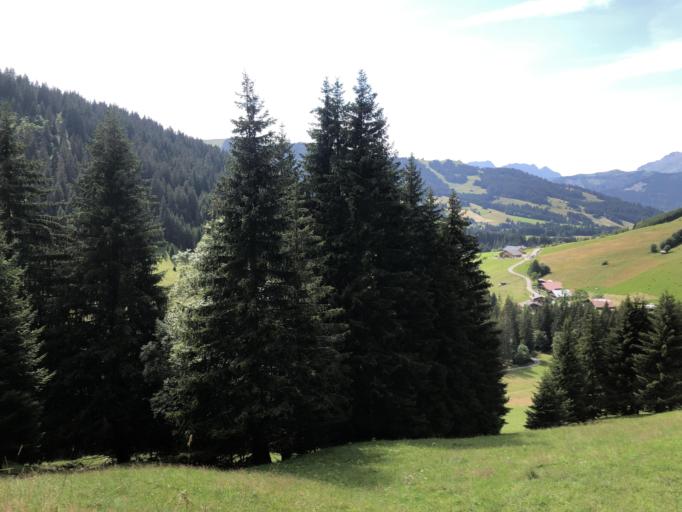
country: FR
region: Rhone-Alpes
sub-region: Departement de la Haute-Savoie
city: Megeve
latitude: 45.8303
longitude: 6.6649
